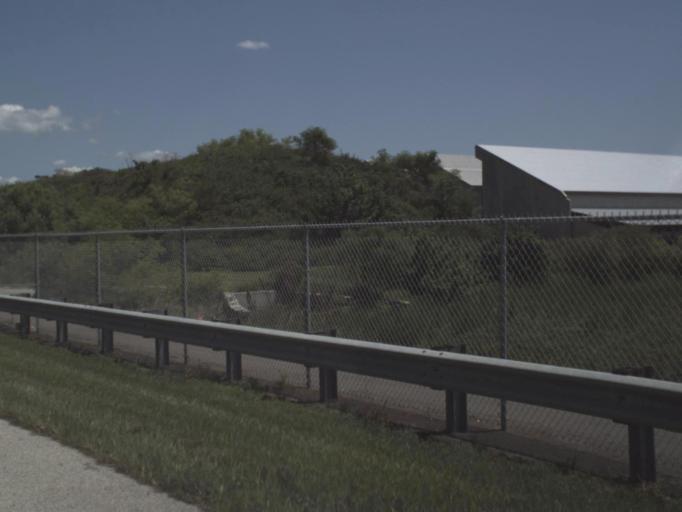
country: US
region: Florida
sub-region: Pinellas County
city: Pinellas Park
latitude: 27.8787
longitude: -82.6825
